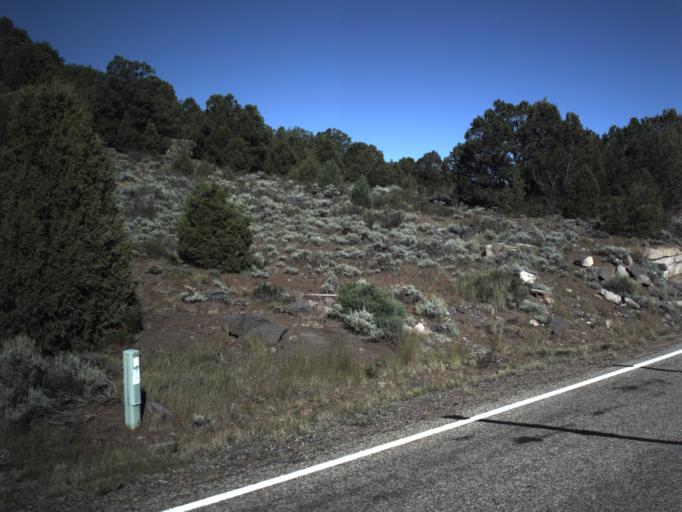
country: US
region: Utah
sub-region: Garfield County
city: Panguitch
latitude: 37.7625
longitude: -112.5268
